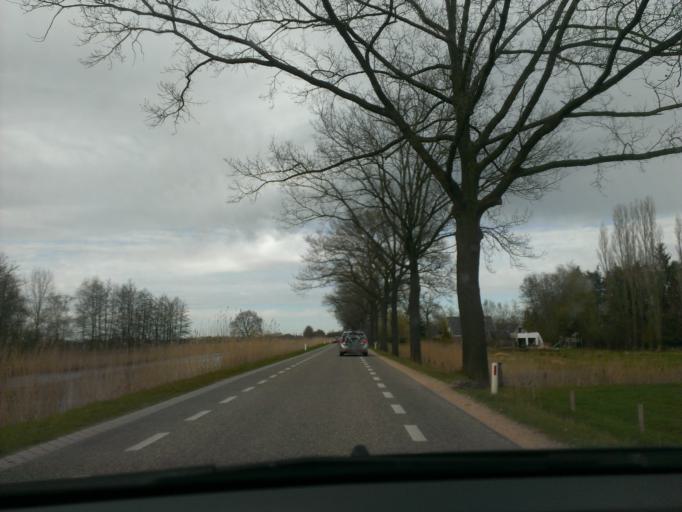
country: NL
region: Gelderland
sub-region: Gemeente Epe
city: Vaassen
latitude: 52.2729
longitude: 5.9892
